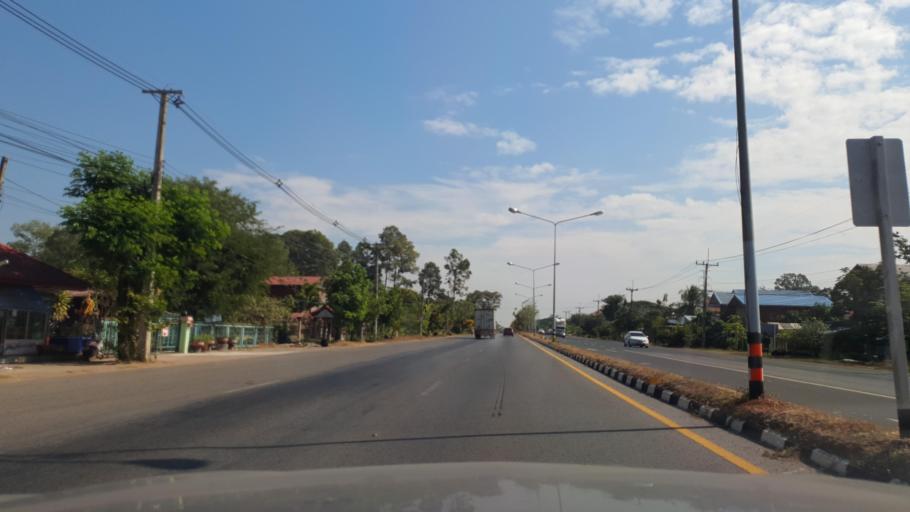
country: TH
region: Maha Sarakham
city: Kantharawichai
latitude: 16.3864
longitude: 103.2438
